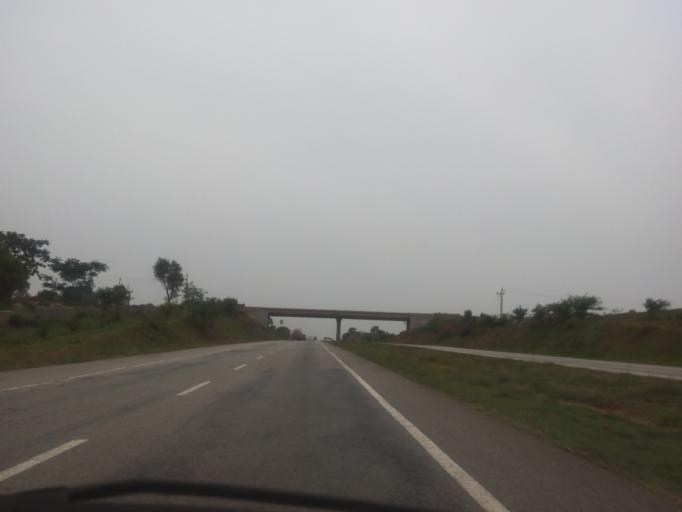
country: IN
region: Karnataka
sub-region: Bangalore Urban
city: Bangalore
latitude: 12.9725
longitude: 77.4714
